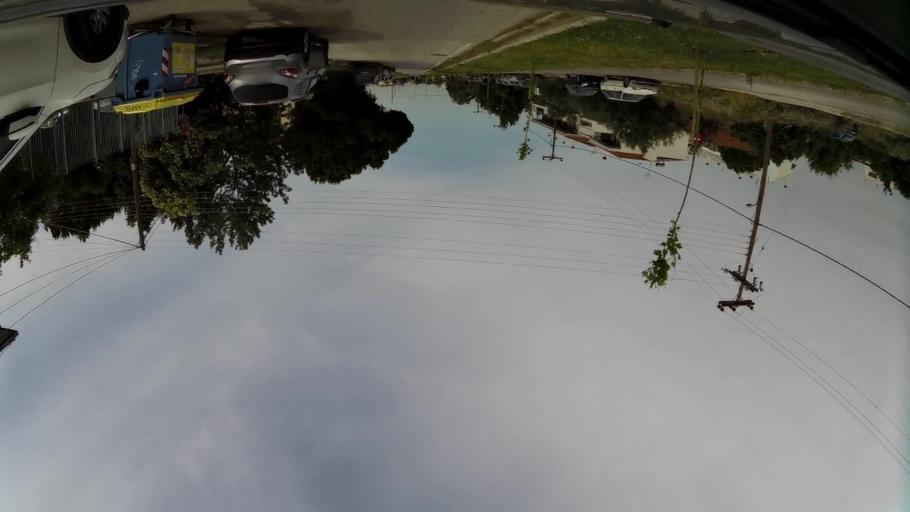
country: GR
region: Central Macedonia
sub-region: Nomos Thessalonikis
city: Thermi
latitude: 40.5481
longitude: 23.0126
